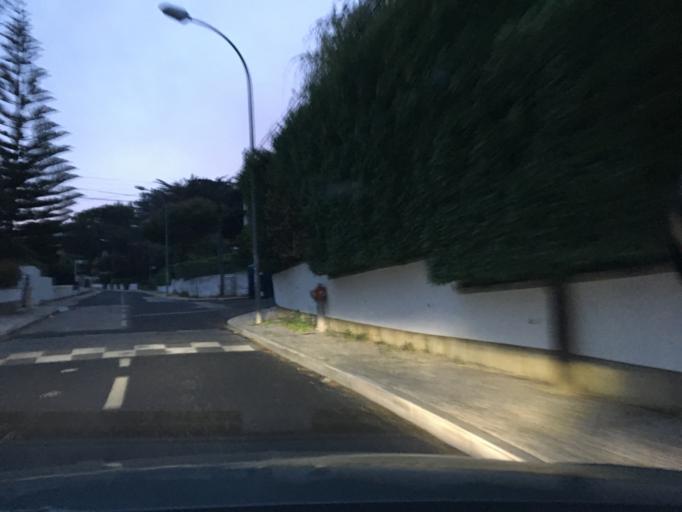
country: PT
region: Lisbon
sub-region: Oeiras
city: Terrugem
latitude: 38.7042
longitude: -9.2795
